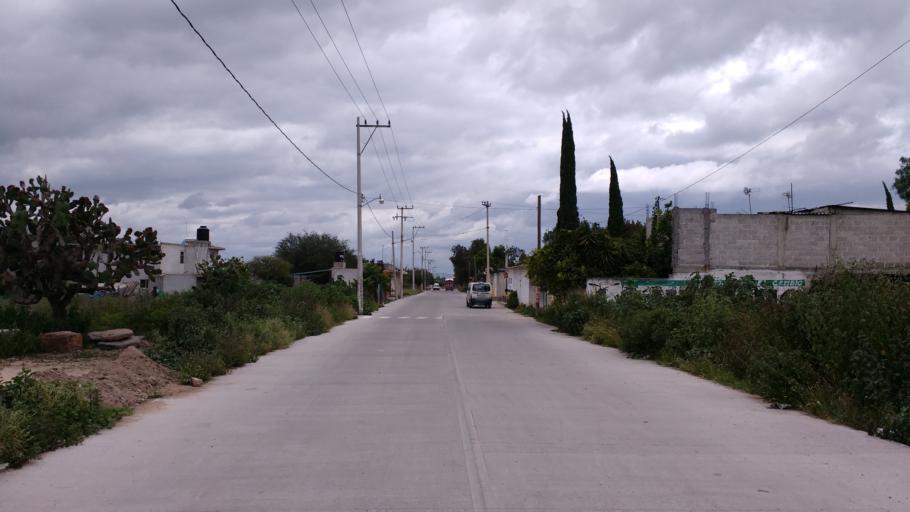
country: MX
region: Hidalgo
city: Mixquiahuala de Juarez
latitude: 20.2318
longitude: -99.2488
